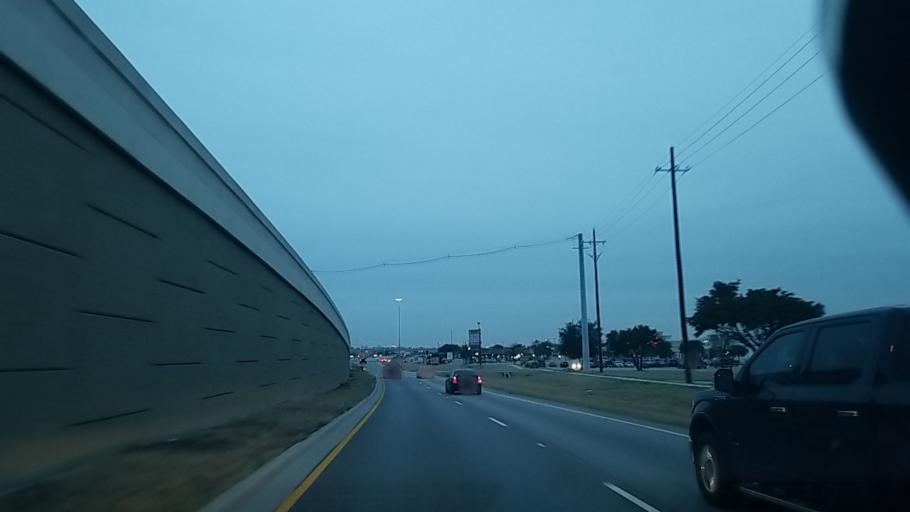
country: US
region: Texas
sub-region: Denton County
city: Lewisville
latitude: 33.0039
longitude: -96.9652
